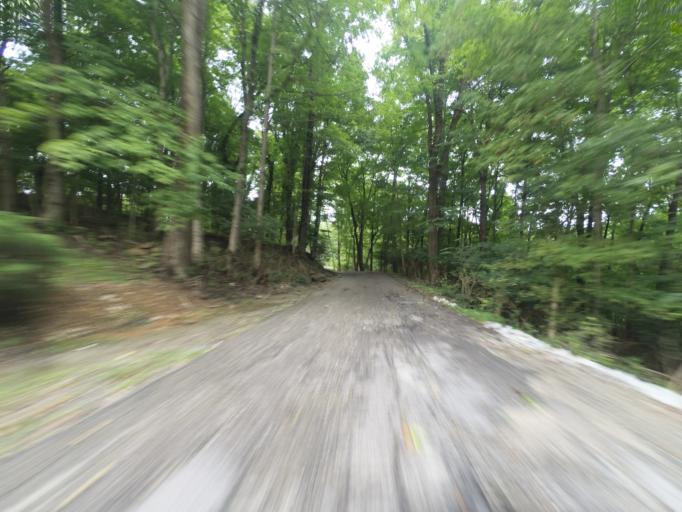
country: US
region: West Virginia
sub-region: Cabell County
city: Huntington
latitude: 38.4008
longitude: -82.4570
